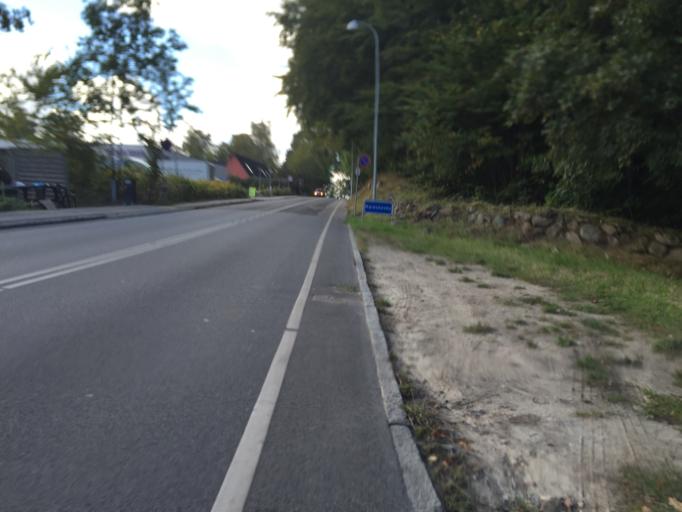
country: DK
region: Capital Region
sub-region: Herlev Kommune
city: Herlev
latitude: 55.7600
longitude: 12.4174
